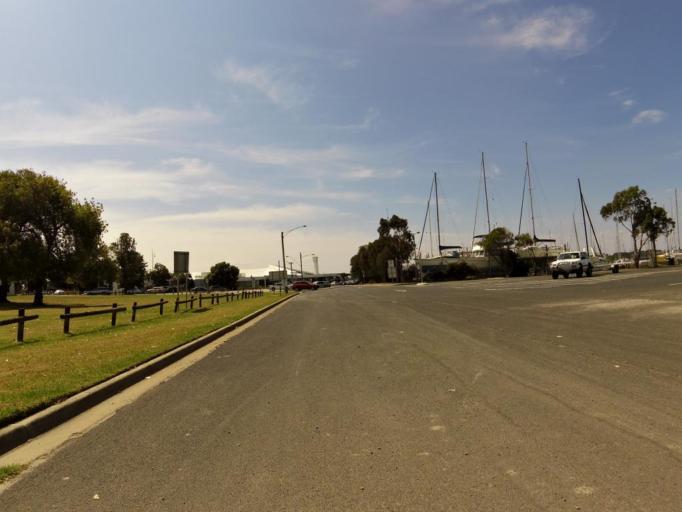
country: AU
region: Victoria
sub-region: Mornington Peninsula
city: Hastings
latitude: -38.3101
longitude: 145.1967
